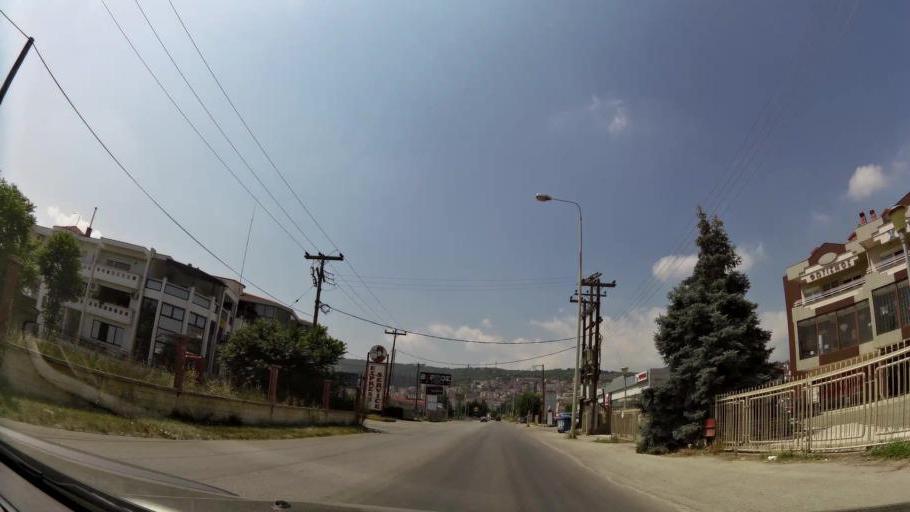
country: GR
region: Central Macedonia
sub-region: Nomos Imathias
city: Veroia
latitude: 40.5218
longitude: 22.2138
